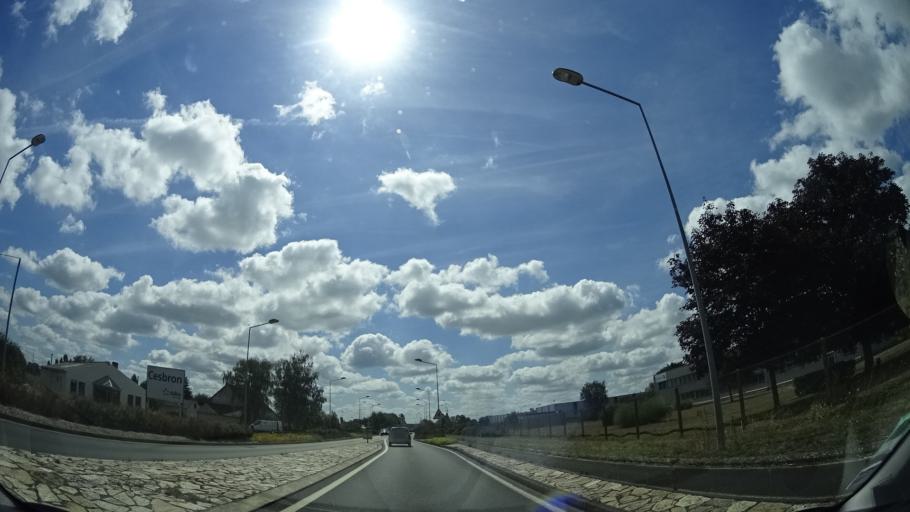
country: FR
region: Pays de la Loire
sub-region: Departement de la Sarthe
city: La Fleche
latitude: 47.7131
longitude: -0.1008
